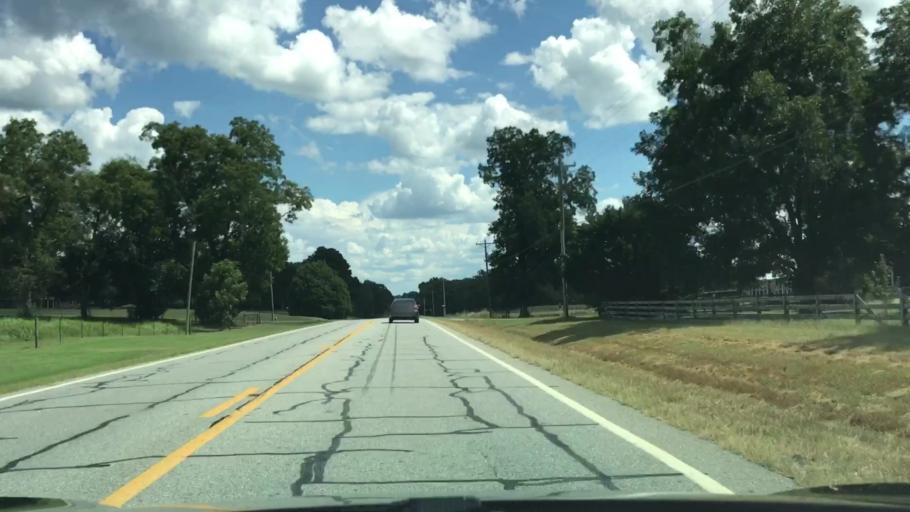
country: US
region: Georgia
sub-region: Oconee County
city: Watkinsville
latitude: 33.8038
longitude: -83.3426
